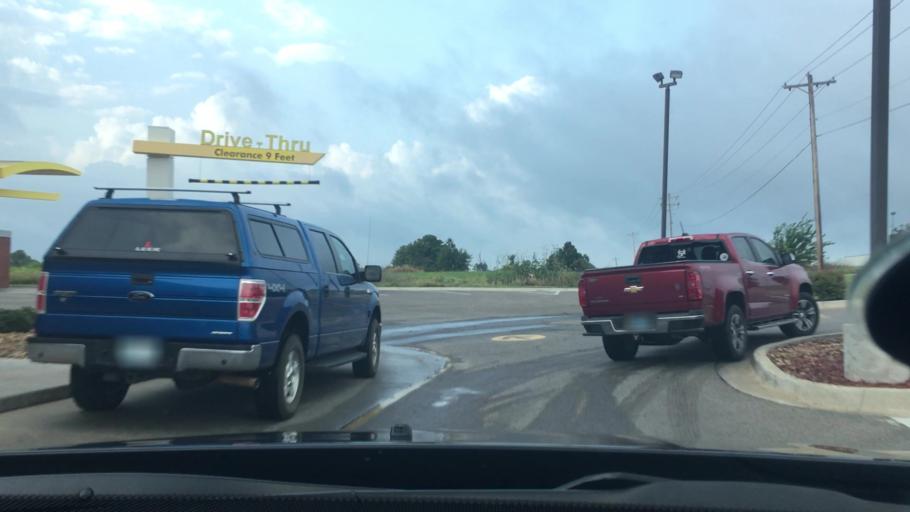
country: US
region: Oklahoma
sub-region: Murray County
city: Sulphur
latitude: 34.5055
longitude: -97.0028
